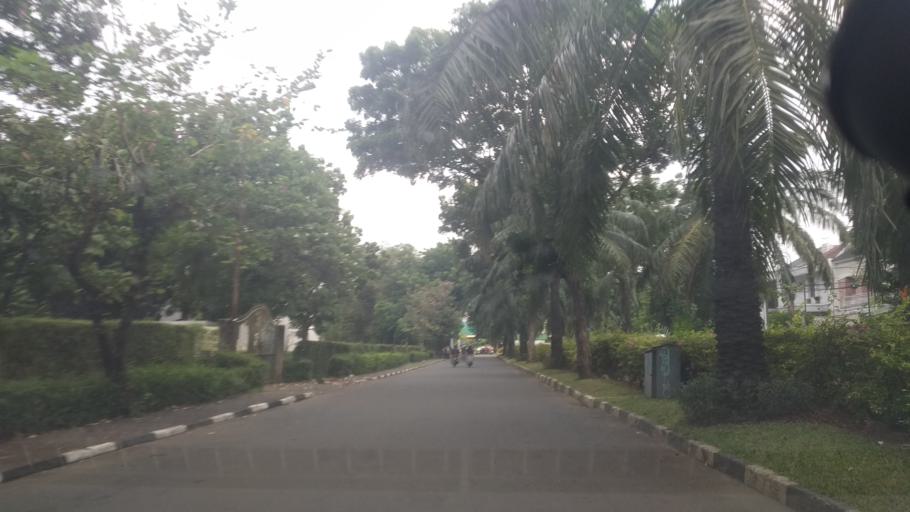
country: ID
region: Banten
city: South Tangerang
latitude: -6.2704
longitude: 106.7475
